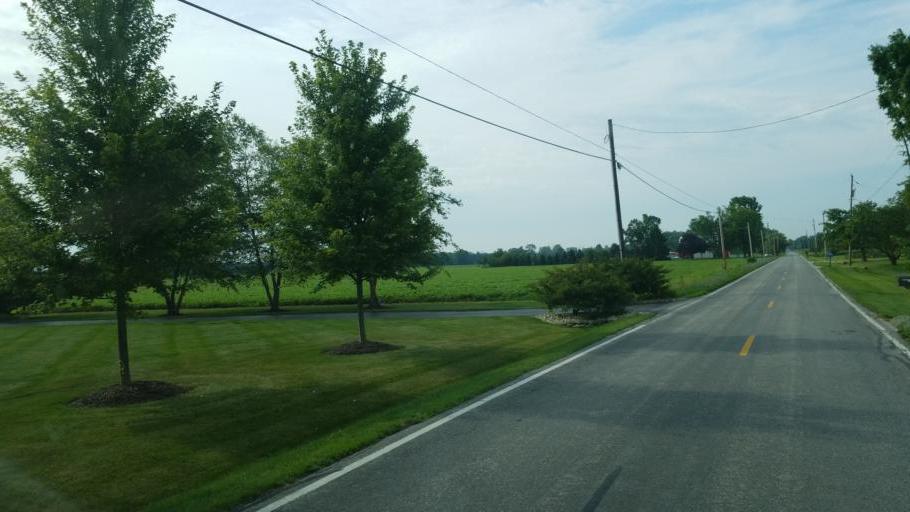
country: US
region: Ohio
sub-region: Union County
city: New California
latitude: 40.2139
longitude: -83.1674
